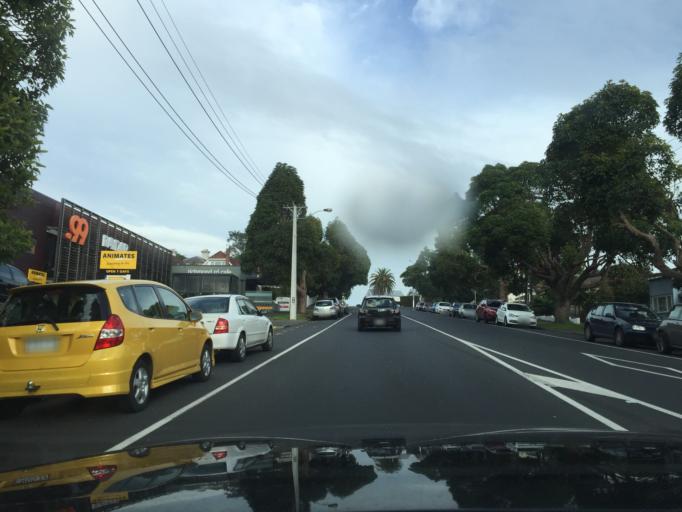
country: NZ
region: Auckland
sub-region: Auckland
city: Auckland
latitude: -36.8548
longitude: 174.7314
